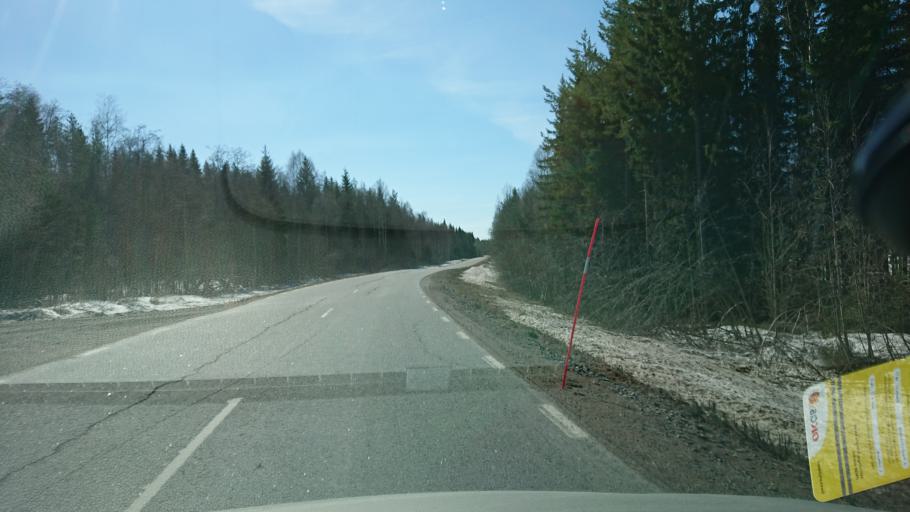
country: SE
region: Vaesternorrland
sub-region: Solleftea Kommun
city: As
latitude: 63.6771
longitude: 16.4324
